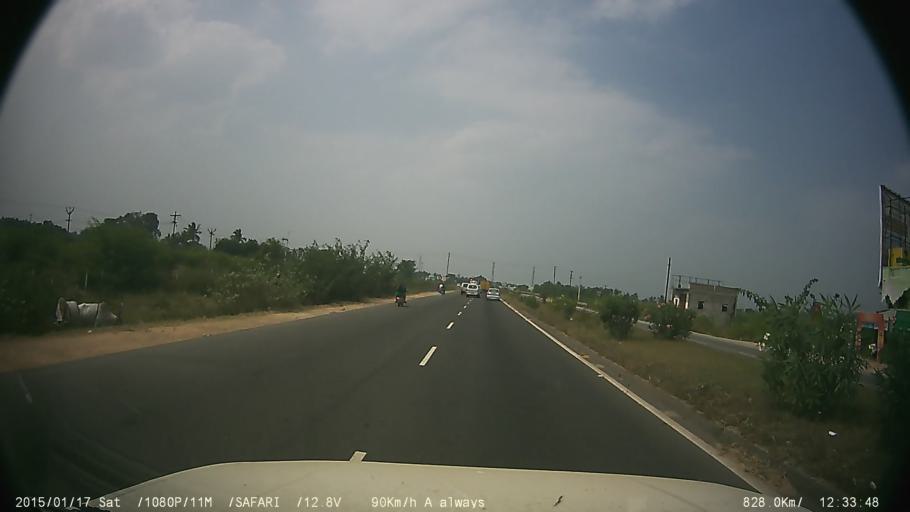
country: IN
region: Tamil Nadu
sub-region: Kancheepuram
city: Kanchipuram
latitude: 12.8736
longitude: 79.6299
